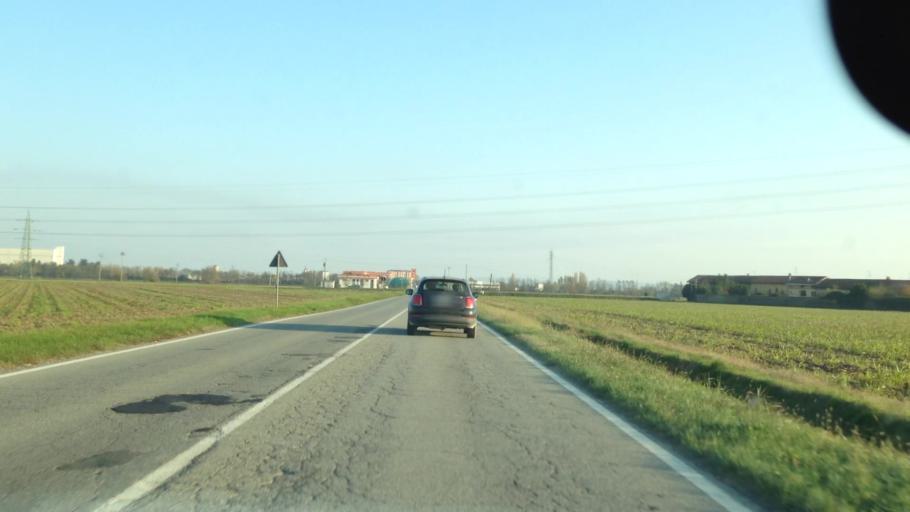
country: IT
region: Piedmont
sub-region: Provincia di Vercelli
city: Livorno Ferraris
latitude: 45.2923
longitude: 8.0521
